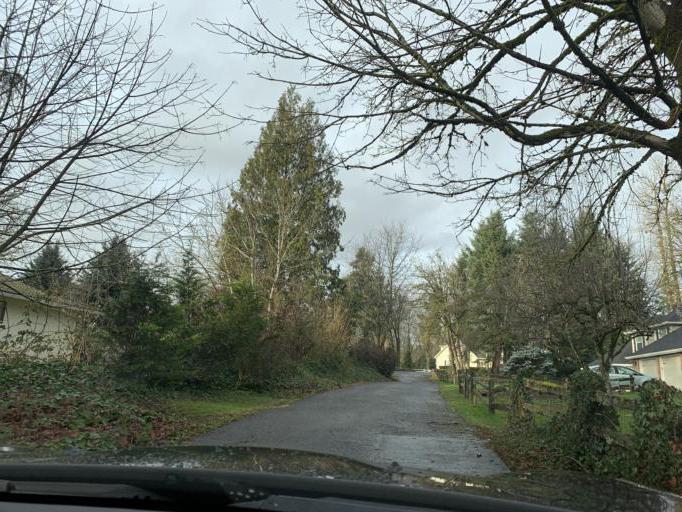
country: US
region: Washington
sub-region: Clark County
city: Mill Plain
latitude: 45.5914
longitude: -122.5100
